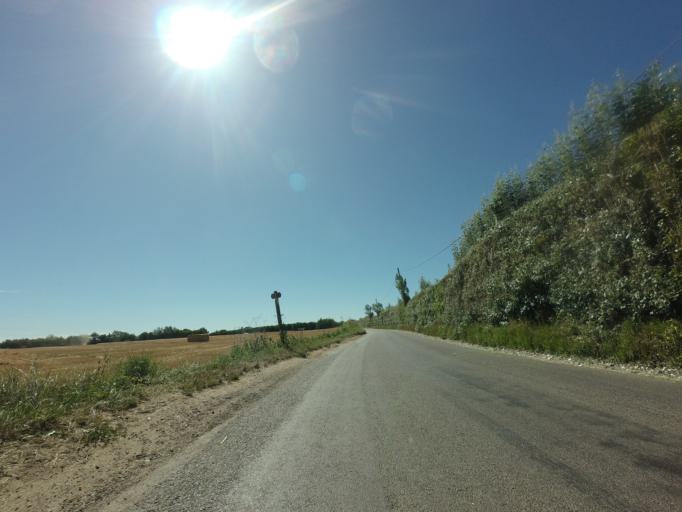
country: GB
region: England
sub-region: Kent
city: Ash
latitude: 51.2818
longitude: 1.2599
